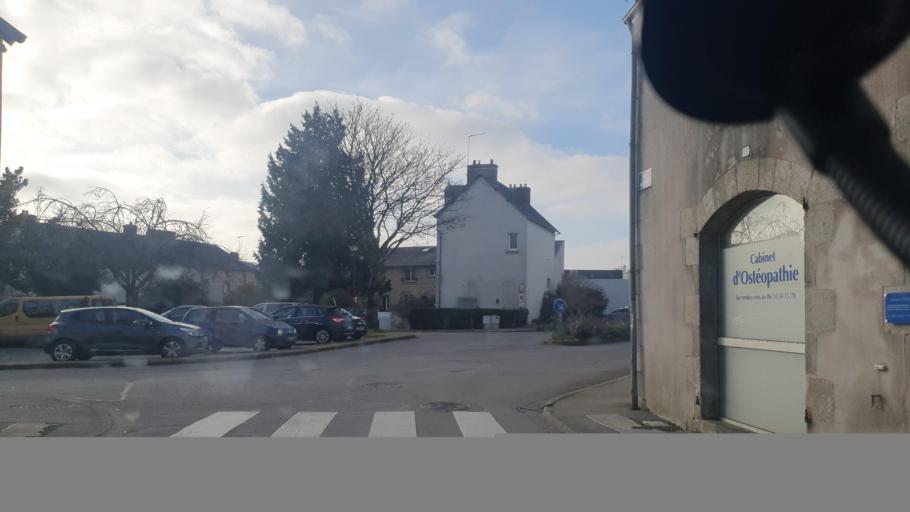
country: FR
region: Brittany
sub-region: Departement du Finistere
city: Briec
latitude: 48.1030
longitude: -3.9993
